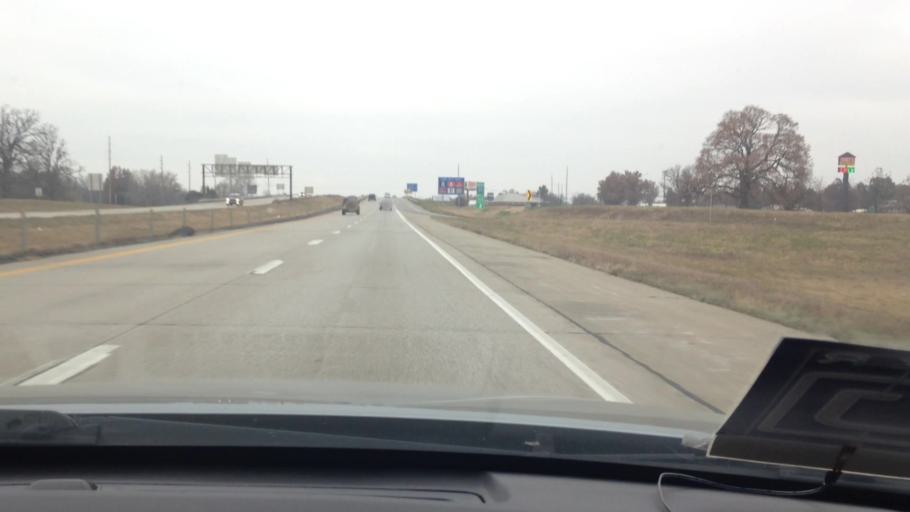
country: US
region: Missouri
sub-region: Cass County
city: Harrisonville
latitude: 38.6506
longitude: -94.3650
